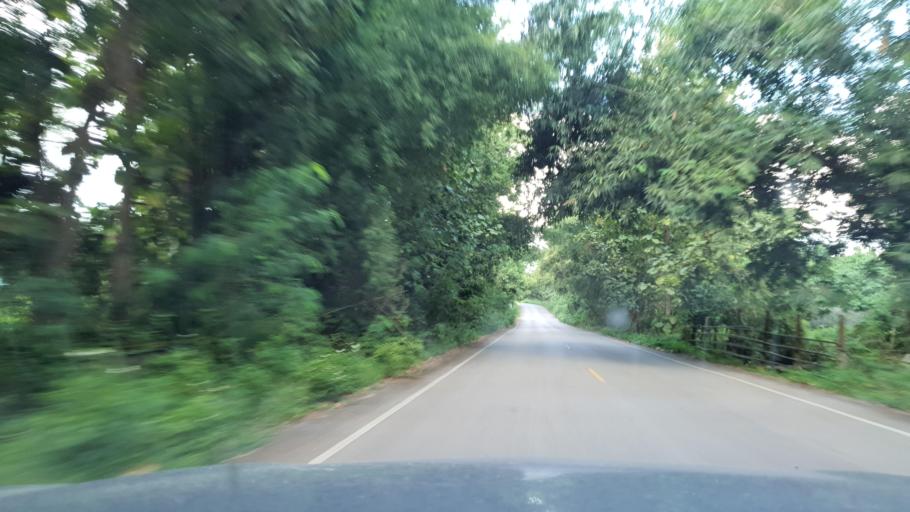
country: TH
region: Phayao
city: Phayao
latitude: 19.0954
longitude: 99.8301
